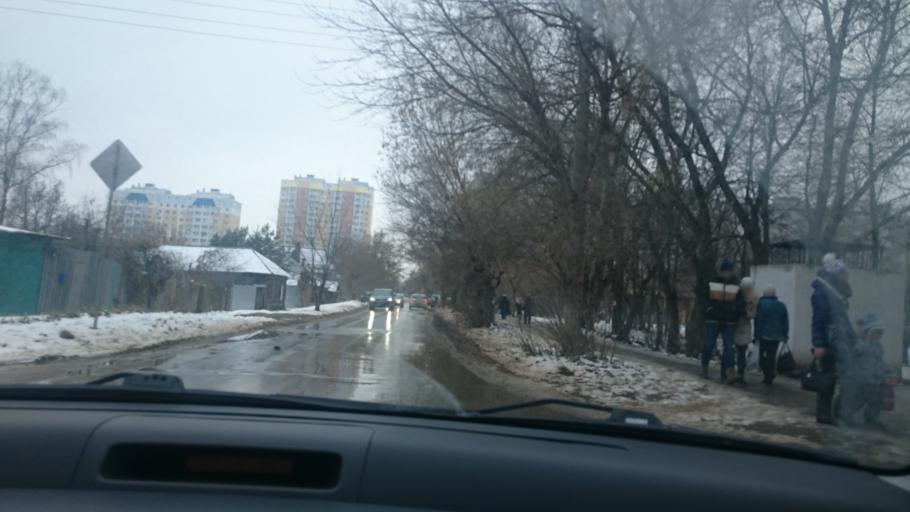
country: RU
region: Tula
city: Tula
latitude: 54.2128
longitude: 37.6085
